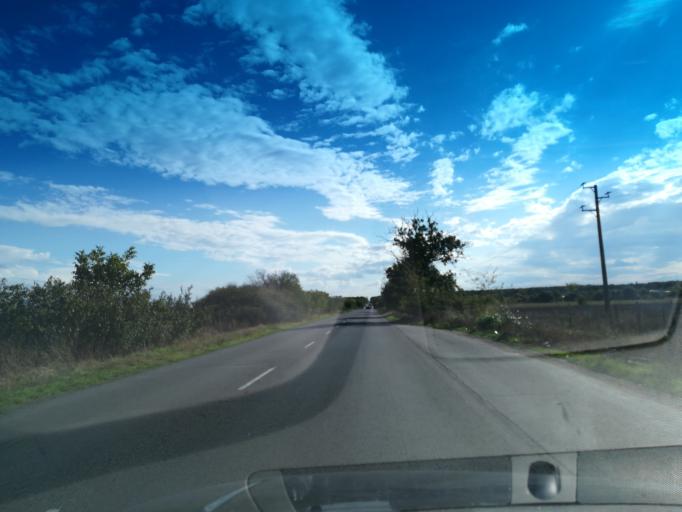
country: BG
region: Stara Zagora
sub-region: Obshtina Stara Zagora
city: Stara Zagora
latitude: 42.3659
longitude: 25.6544
